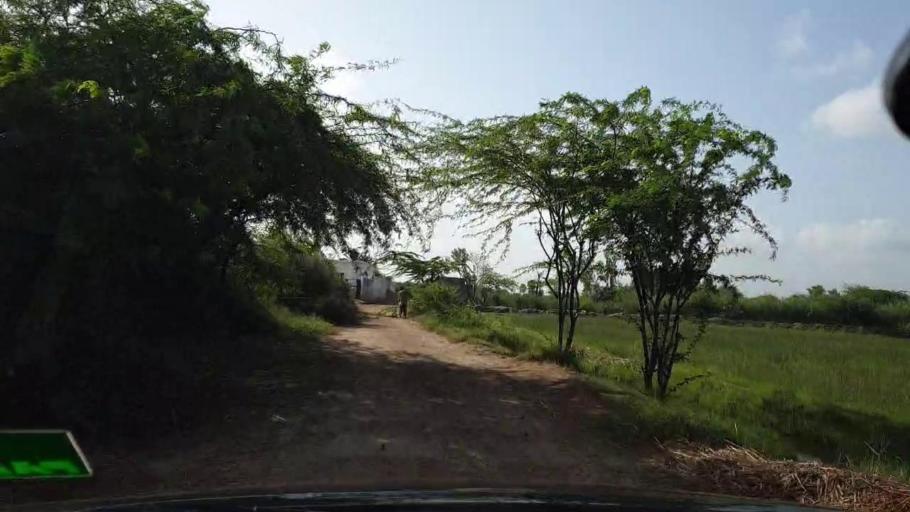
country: PK
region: Sindh
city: Tando Bago
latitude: 24.6442
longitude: 69.0471
